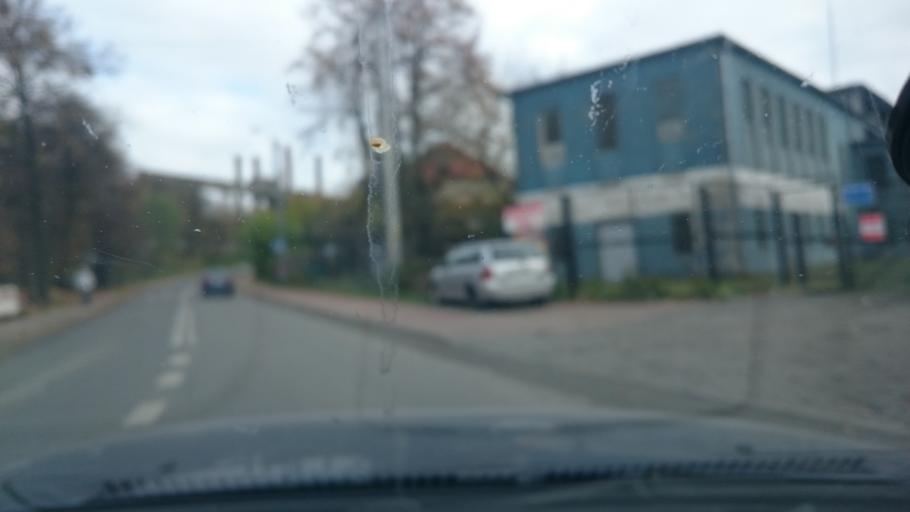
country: PL
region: Silesian Voivodeship
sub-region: Powiat bedzinski
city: Strzyzowice
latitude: 50.3513
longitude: 19.0849
